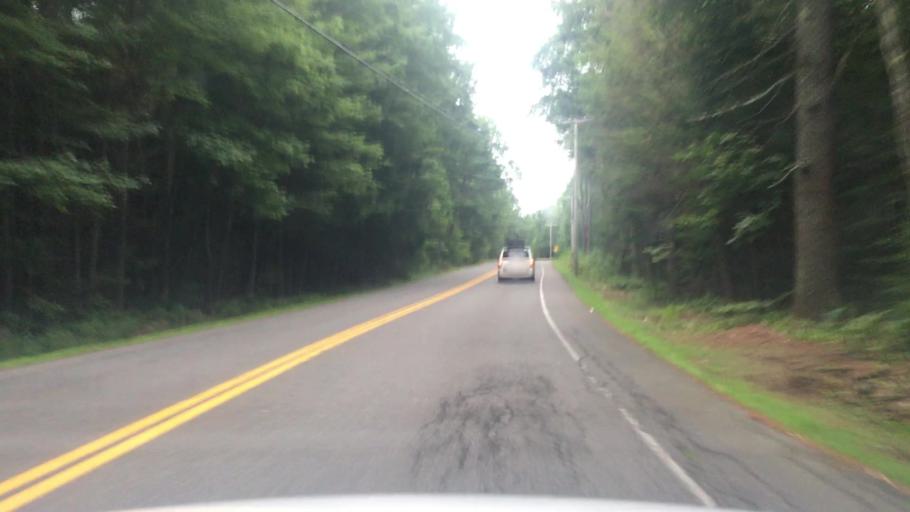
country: US
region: Maine
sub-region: York County
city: Wells Beach Station
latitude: 43.3163
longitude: -70.5984
